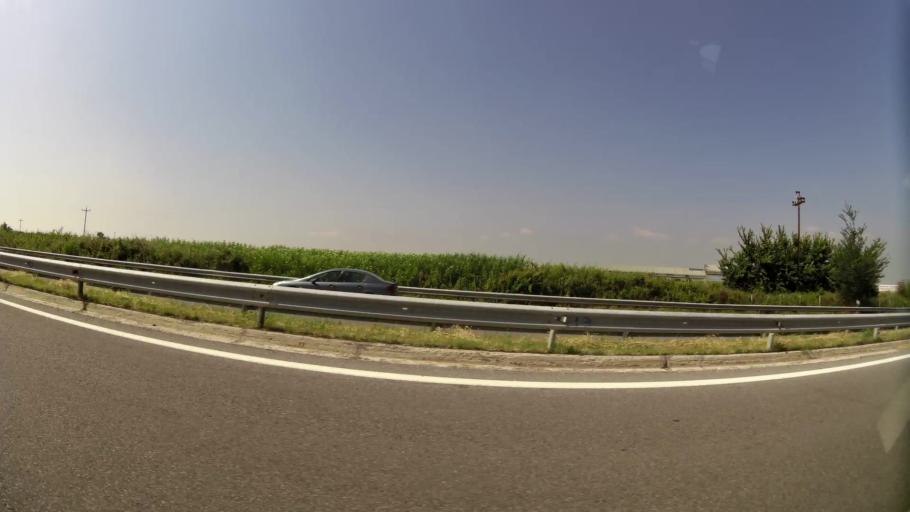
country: GR
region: Central Macedonia
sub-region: Nomos Imathias
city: Kleidi
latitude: 40.5581
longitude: 22.5917
